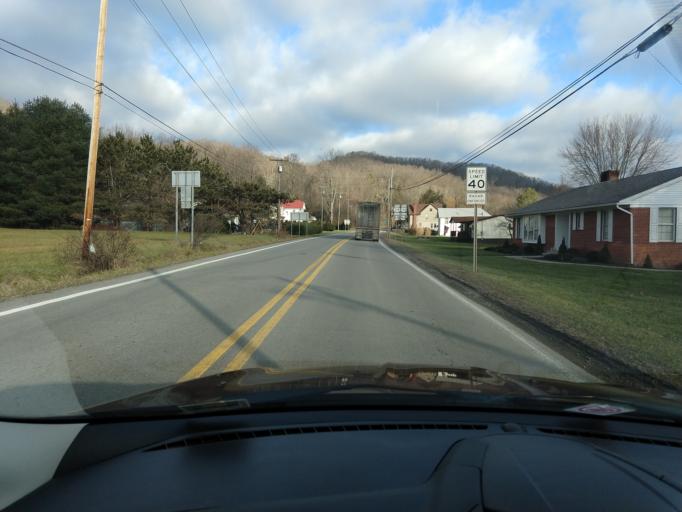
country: US
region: West Virginia
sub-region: Randolph County
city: Elkins
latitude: 38.7117
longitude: -79.9791
